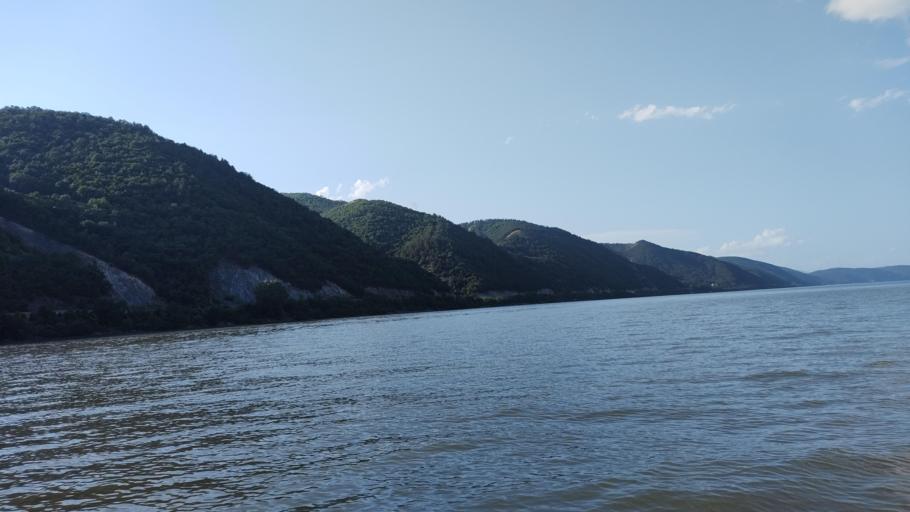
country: RO
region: Mehedinti
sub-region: Comuna Svinita
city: Svinita
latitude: 44.4945
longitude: 22.1882
